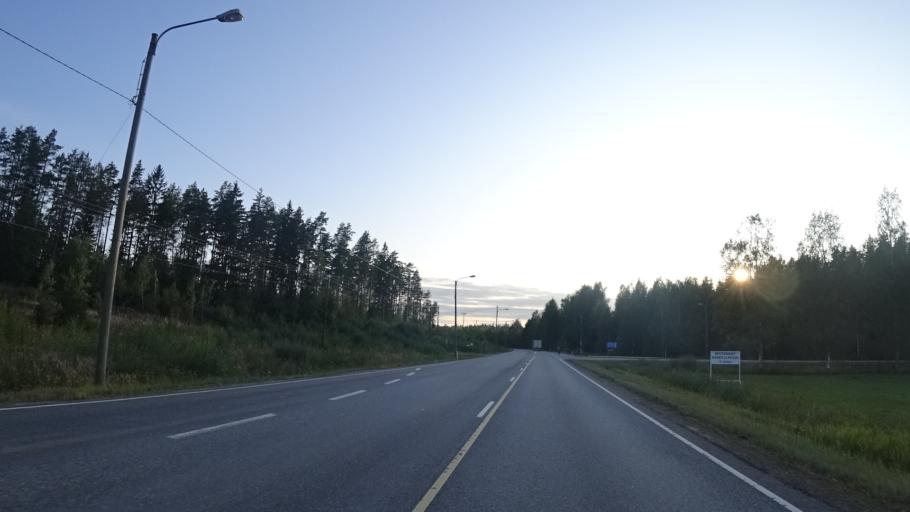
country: FI
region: South Karelia
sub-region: Lappeenranta
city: Ylaemaa
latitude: 60.7897
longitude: 28.0104
